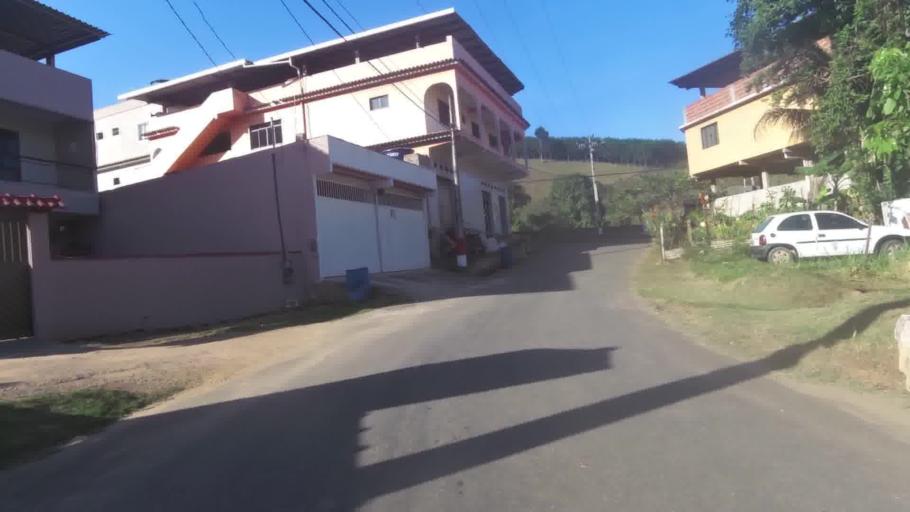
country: BR
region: Espirito Santo
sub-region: Iconha
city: Iconha
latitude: -20.7296
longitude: -40.7787
